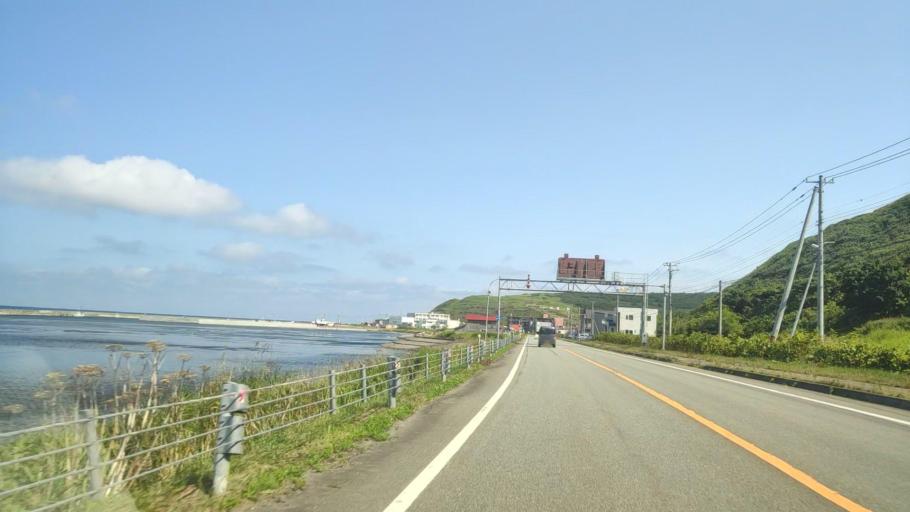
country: JP
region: Hokkaido
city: Makubetsu
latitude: 45.4825
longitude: 141.8798
